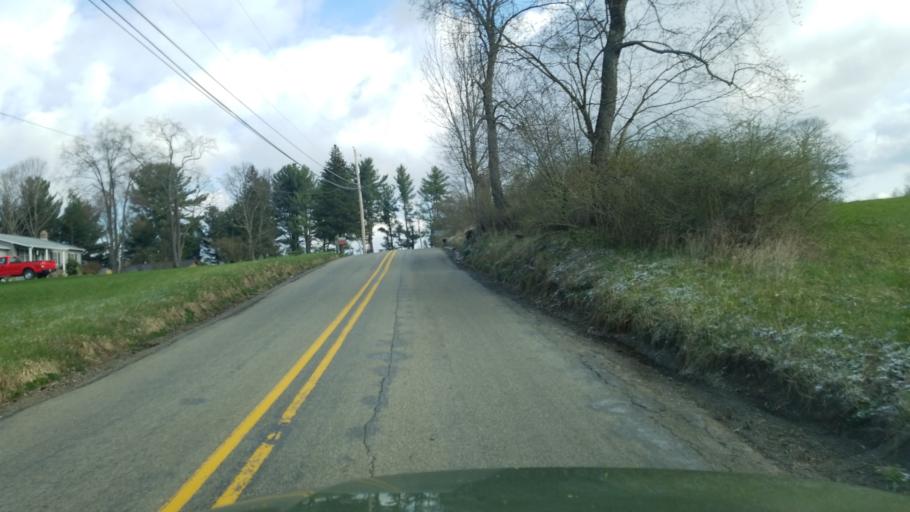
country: US
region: Pennsylvania
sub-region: Jefferson County
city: Brockway
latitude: 41.2739
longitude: -78.8430
